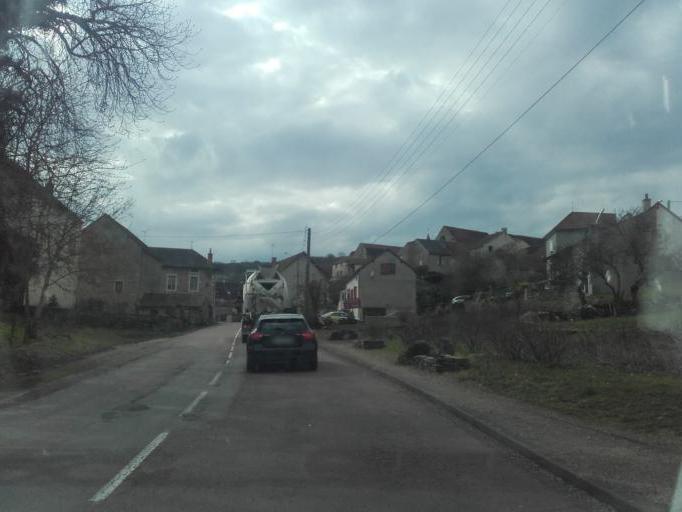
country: FR
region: Bourgogne
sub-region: Departement de la Cote-d'Or
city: Nolay
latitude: 46.9573
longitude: 4.6810
